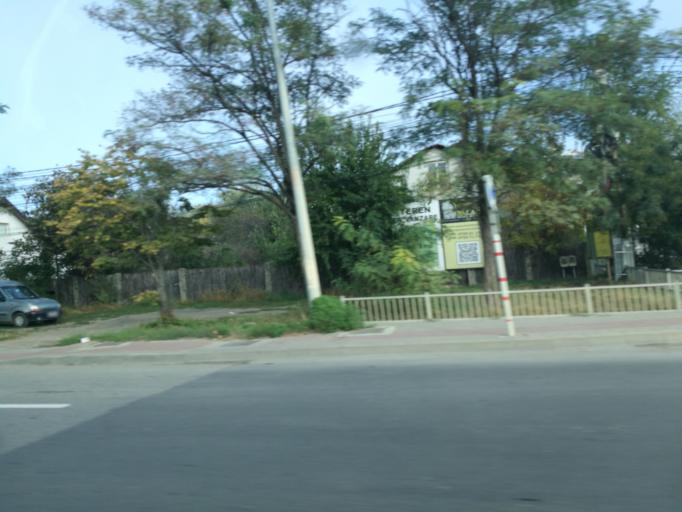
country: RO
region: Iasi
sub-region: Comuna Miroslava
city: Miroslava
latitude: 47.1726
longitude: 27.5258
